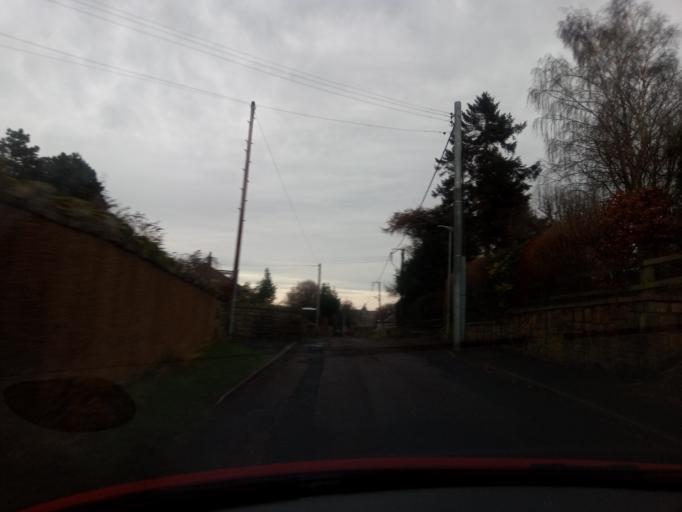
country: GB
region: England
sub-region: Northumberland
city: Wooler
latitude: 55.5481
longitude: -2.0233
